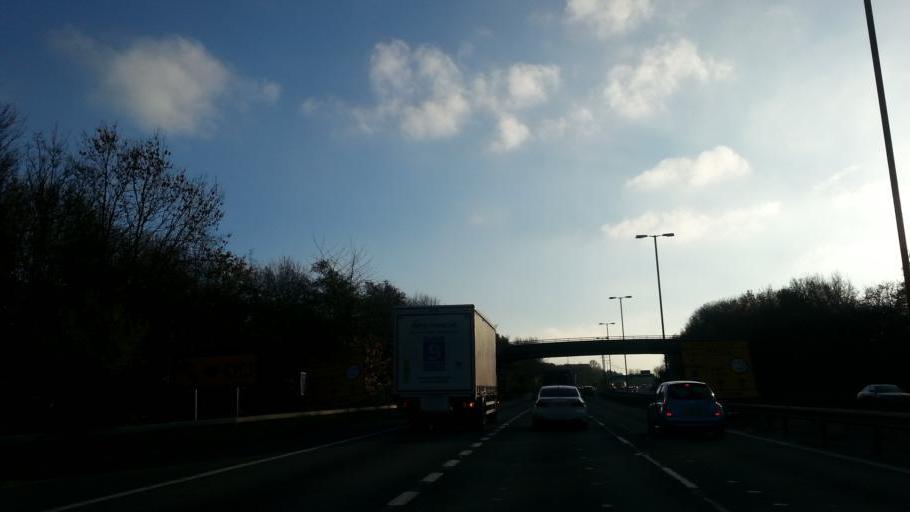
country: GB
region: England
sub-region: Sandwell
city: Smethwick
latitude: 52.5205
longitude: -1.9706
